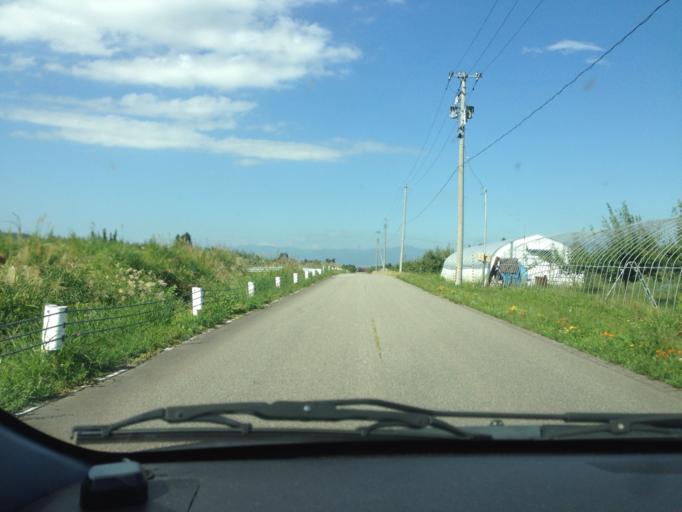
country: JP
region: Fukushima
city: Kitakata
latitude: 37.4358
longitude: 139.8085
